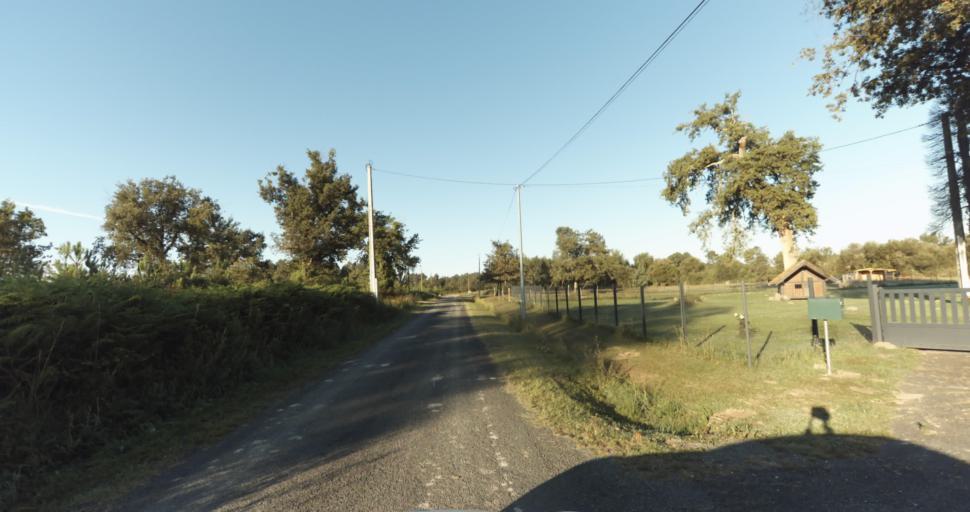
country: FR
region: Aquitaine
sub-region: Departement de la Gironde
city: Bazas
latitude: 44.4084
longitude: -0.2454
